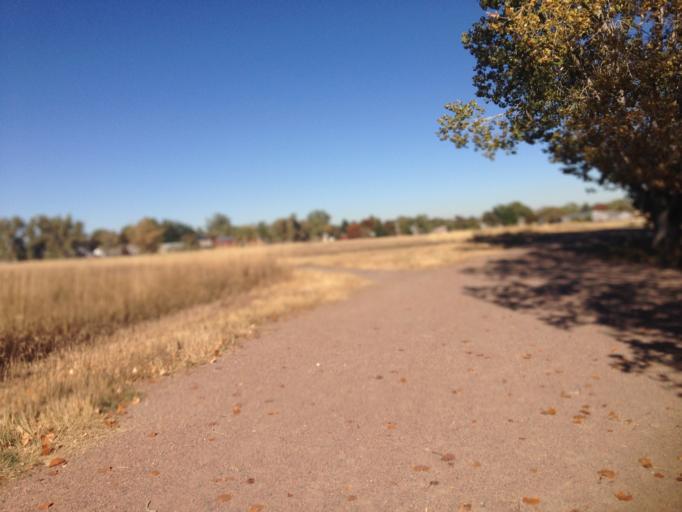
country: US
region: Colorado
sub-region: Boulder County
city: Louisville
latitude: 39.9700
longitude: -105.1441
